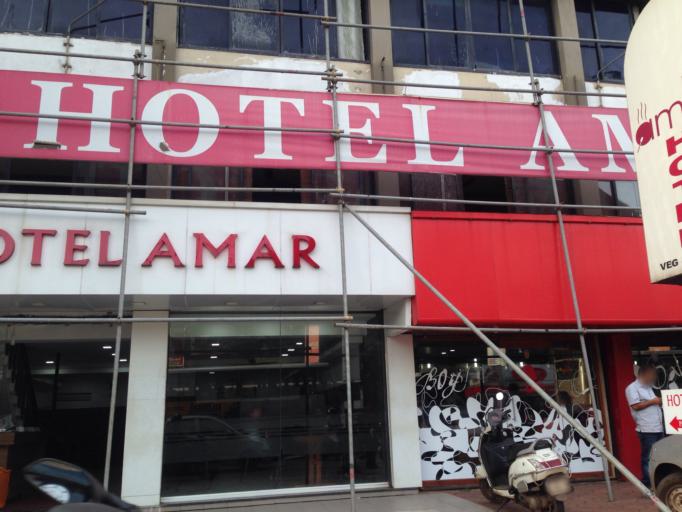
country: IN
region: Kerala
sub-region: Kozhikode
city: Kozhikode
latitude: 11.2595
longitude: 75.7870
